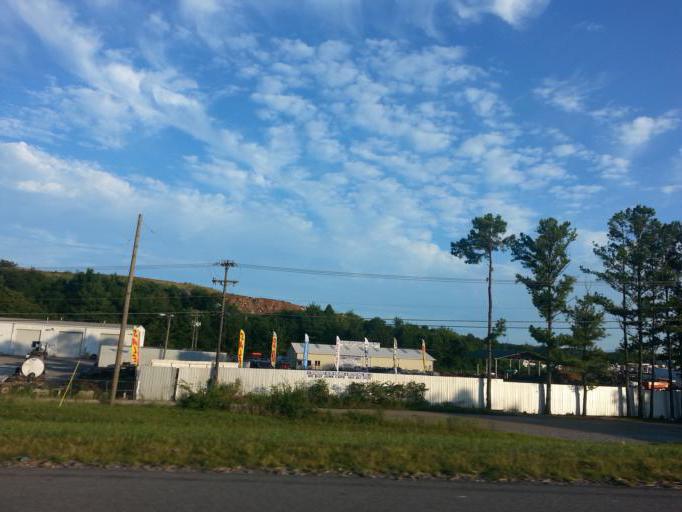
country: US
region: Tennessee
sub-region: Knox County
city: Mascot
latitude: 36.0477
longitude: -83.8065
